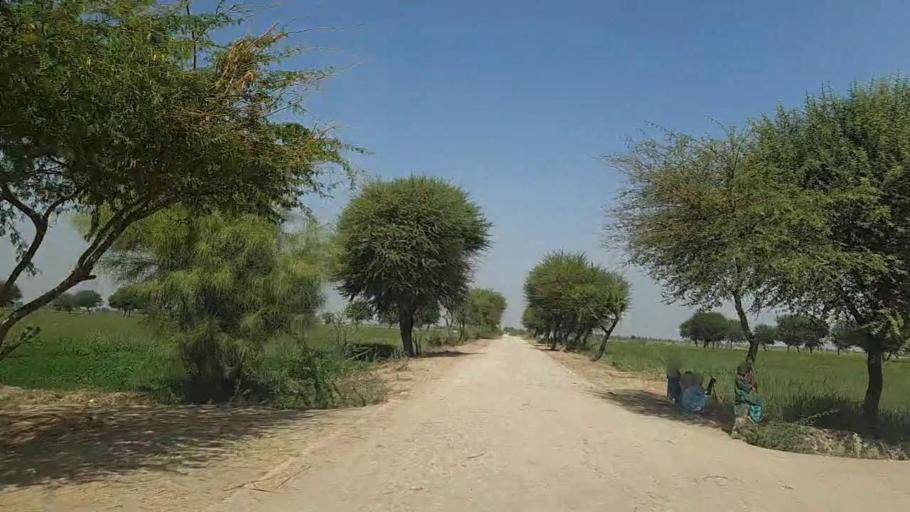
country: PK
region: Sindh
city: Samaro
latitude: 25.1886
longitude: 69.4041
